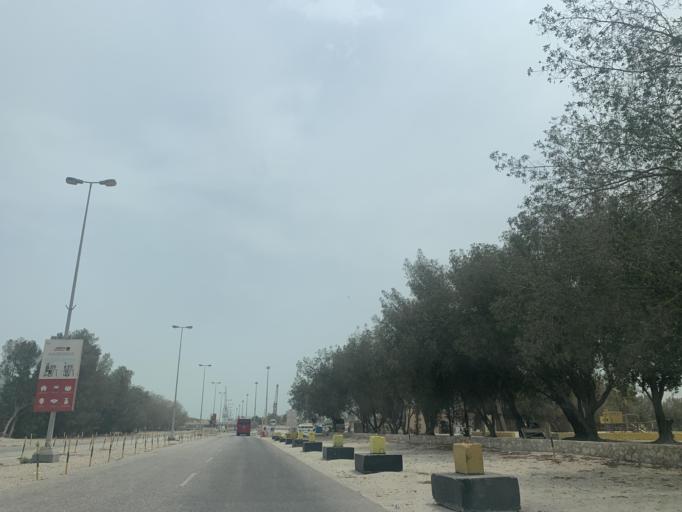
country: BH
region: Muharraq
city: Al Hadd
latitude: 26.1969
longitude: 50.6630
